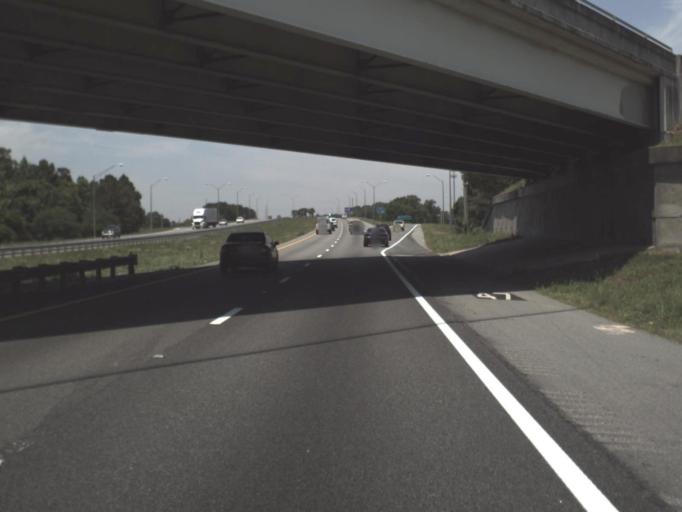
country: US
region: Florida
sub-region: Duval County
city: Jacksonville
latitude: 30.3370
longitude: -81.5375
